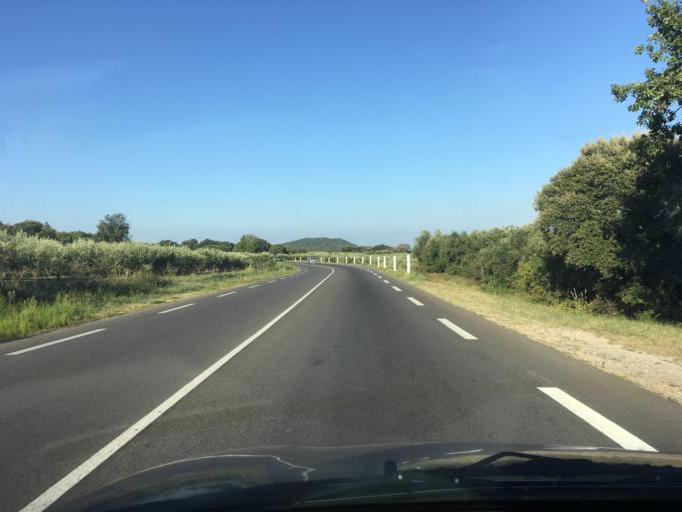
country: FR
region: Languedoc-Roussillon
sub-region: Departement du Gard
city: Bezouce
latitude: 43.8897
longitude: 4.5056
